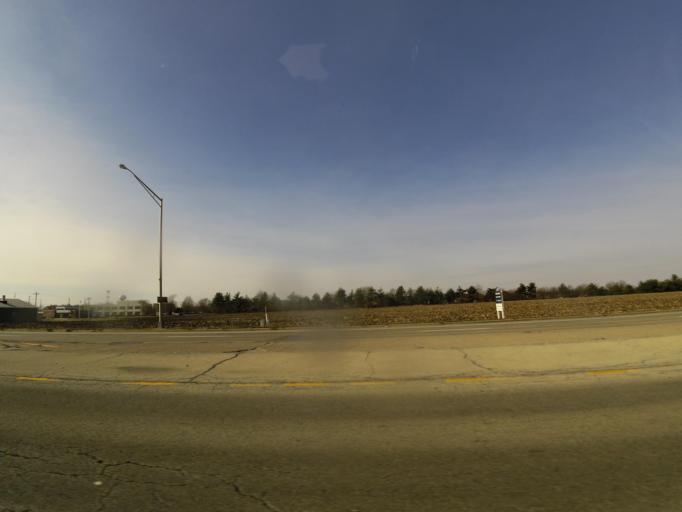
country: US
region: Illinois
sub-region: Macon County
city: Forsyth
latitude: 39.9251
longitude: -88.9554
